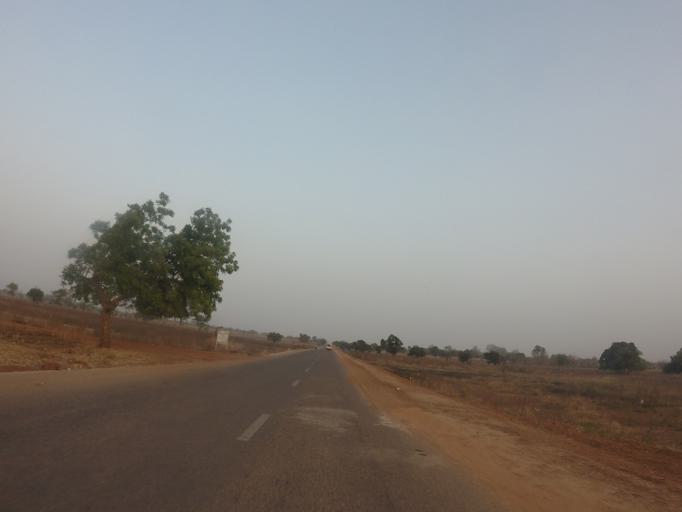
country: GH
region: Northern
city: Tamale
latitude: 9.4416
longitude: -1.1047
